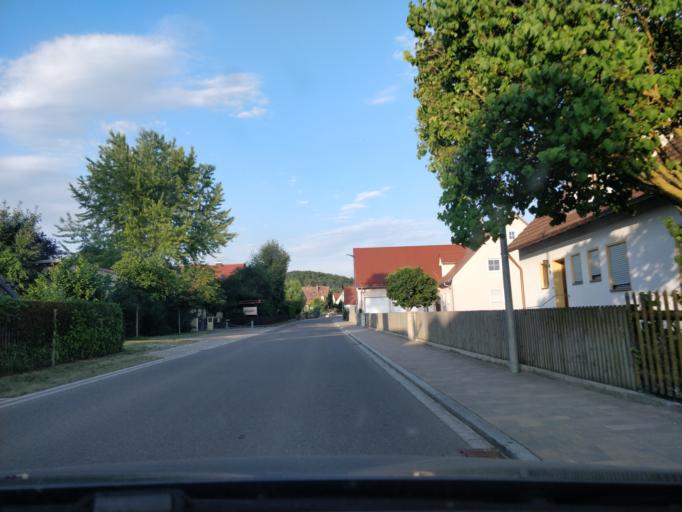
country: DE
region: Bavaria
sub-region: Swabia
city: Ederheim
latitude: 48.8090
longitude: 10.4663
